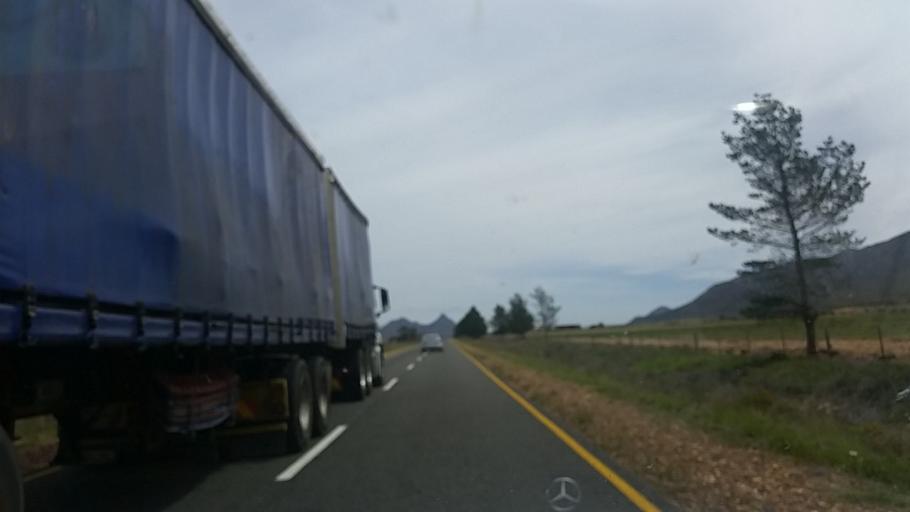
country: ZA
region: Western Cape
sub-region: Eden District Municipality
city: George
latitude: -33.8160
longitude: 22.5151
